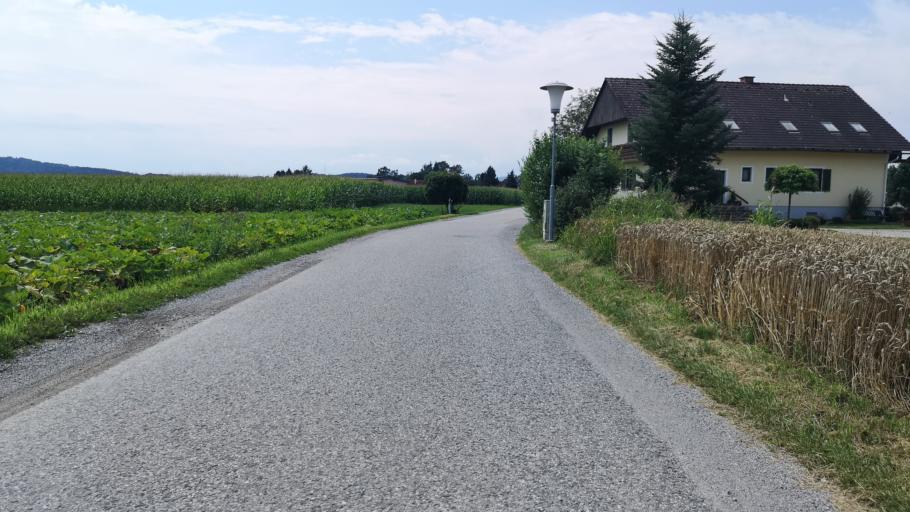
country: AT
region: Styria
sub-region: Politischer Bezirk Leibnitz
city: Weitendorf
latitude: 46.9038
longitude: 15.4774
